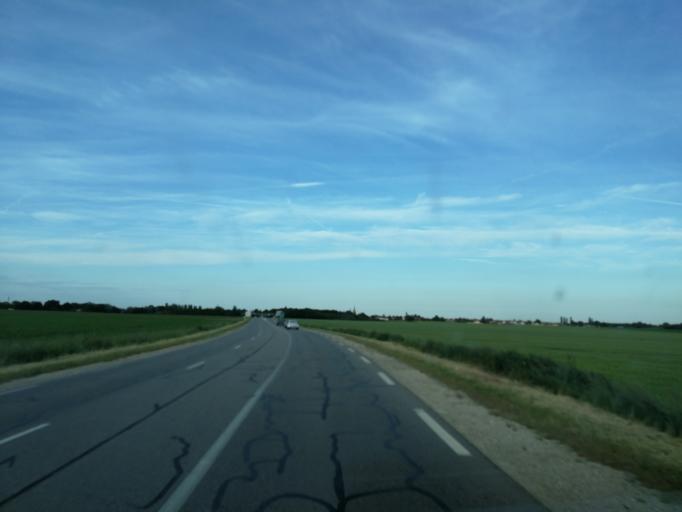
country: FR
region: Ile-de-France
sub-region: Departement des Yvelines
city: Ablis
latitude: 48.5142
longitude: 1.8151
